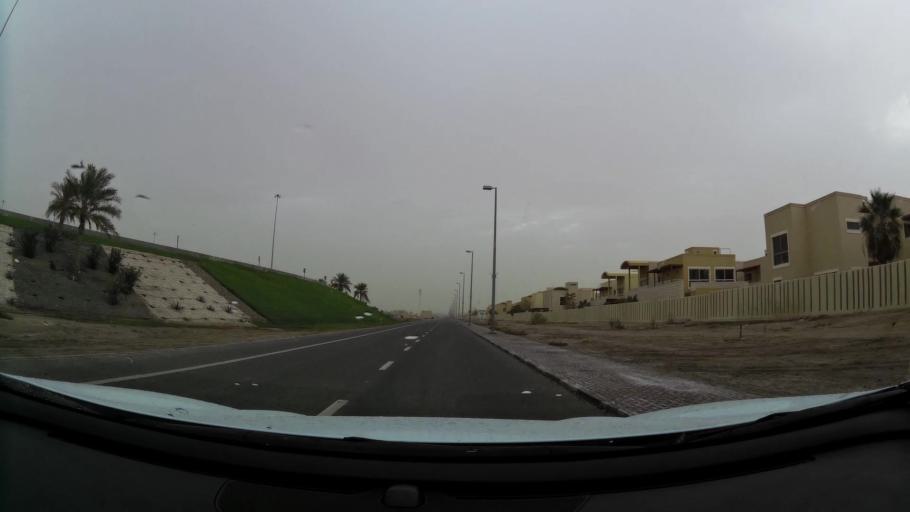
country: AE
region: Abu Dhabi
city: Abu Dhabi
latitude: 24.4385
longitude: 54.5852
